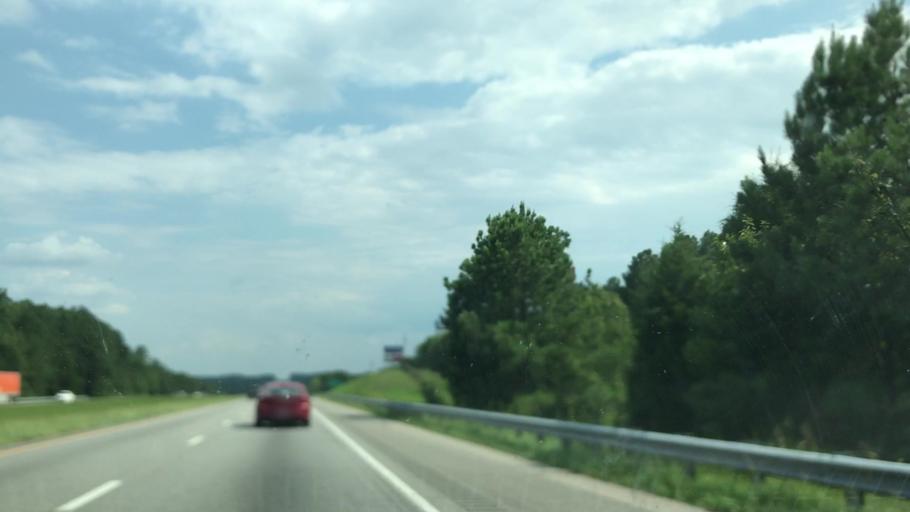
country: US
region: South Carolina
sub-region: Chester County
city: Great Falls
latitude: 34.5986
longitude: -81.0173
